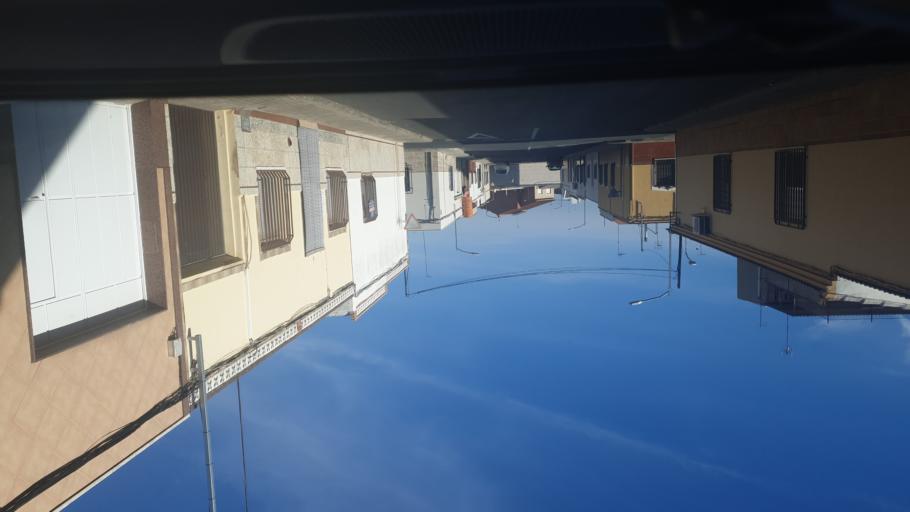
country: ES
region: Castille-La Mancha
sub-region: Provincia de Ciudad Real
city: Tomelloso
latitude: 39.1546
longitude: -3.0091
